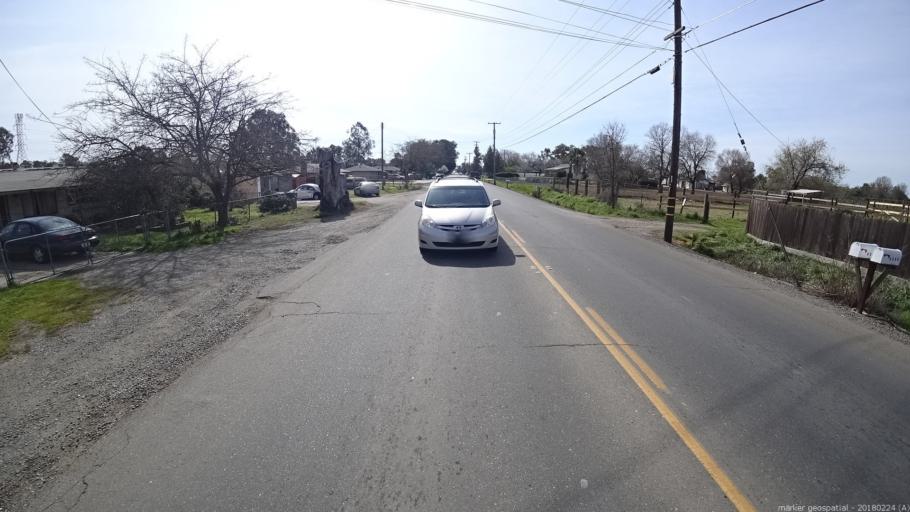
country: US
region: California
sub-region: Sacramento County
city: Rio Linda
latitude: 38.6830
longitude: -121.4291
